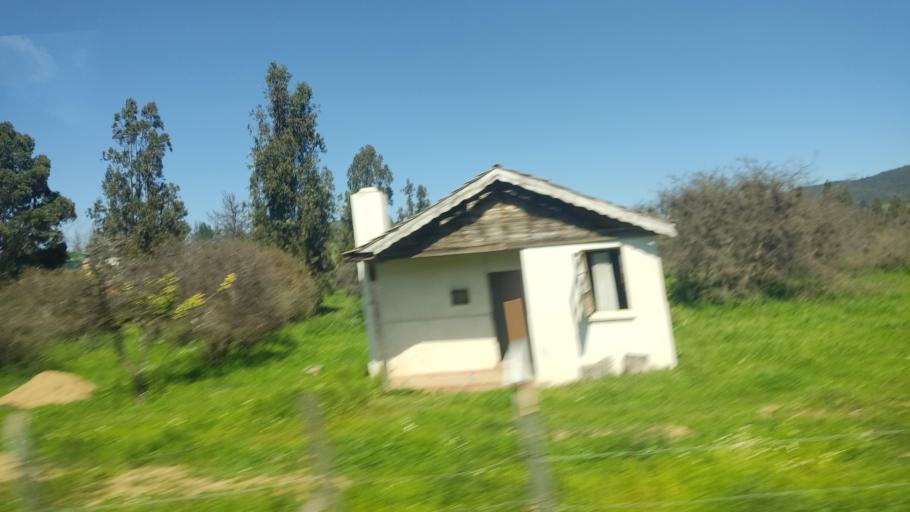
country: CL
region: Valparaiso
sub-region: Provincia de Marga Marga
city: Villa Alemana
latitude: -33.1516
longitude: -71.3370
